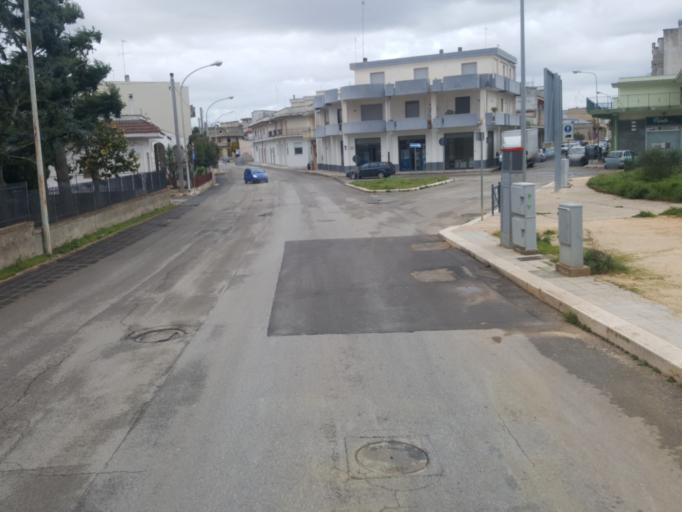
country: IT
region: Apulia
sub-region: Provincia di Bari
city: Turi
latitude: 40.9192
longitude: 17.0286
